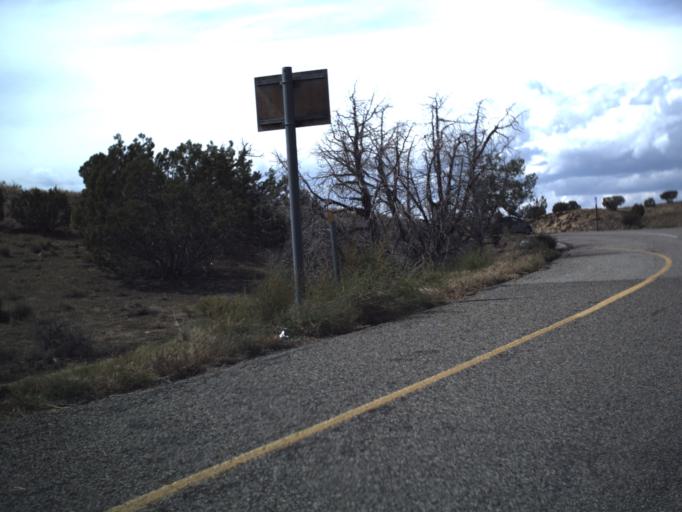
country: US
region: Colorado
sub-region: Mesa County
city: Loma
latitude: 39.1886
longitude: -109.1156
